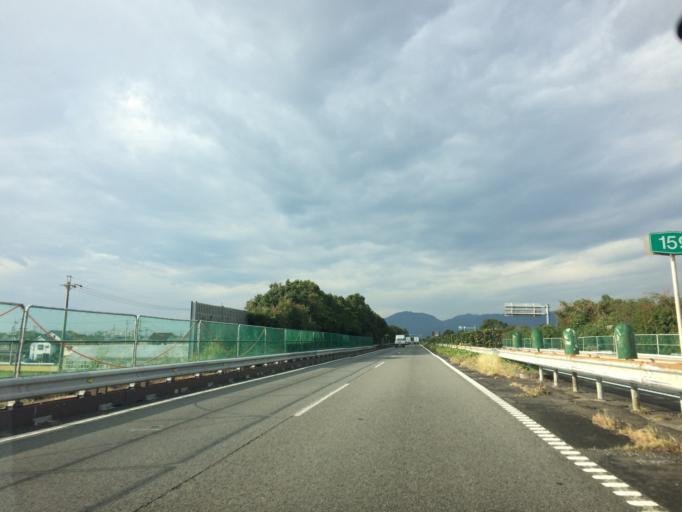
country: JP
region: Shizuoka
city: Shizuoka-shi
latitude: 34.9602
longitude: 138.4202
